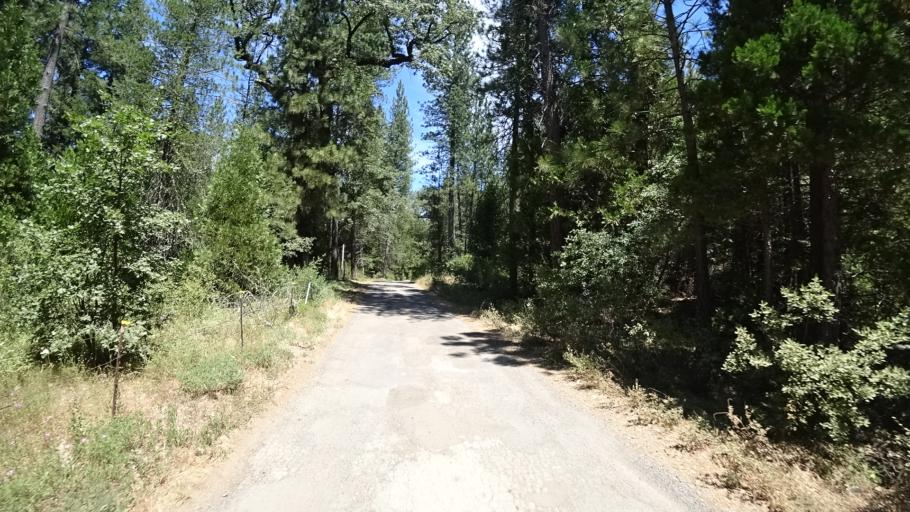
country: US
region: California
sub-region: Calaveras County
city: Arnold
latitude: 38.2558
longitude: -120.4222
